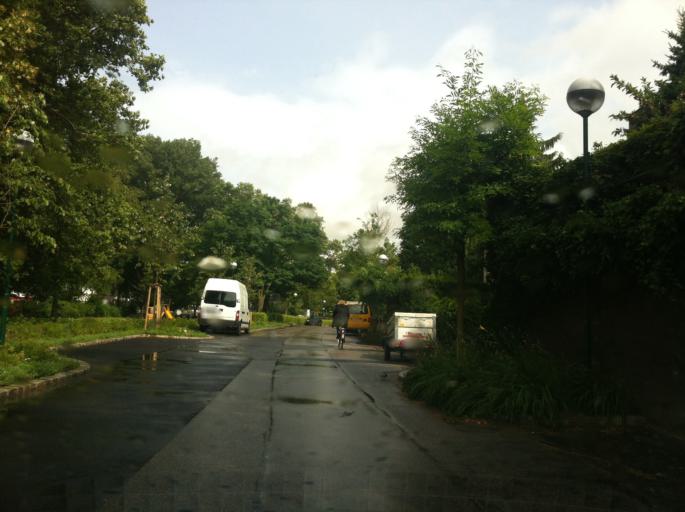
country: AT
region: Lower Austria
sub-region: Politischer Bezirk Tulln
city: Tulln
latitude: 48.3334
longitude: 16.0596
